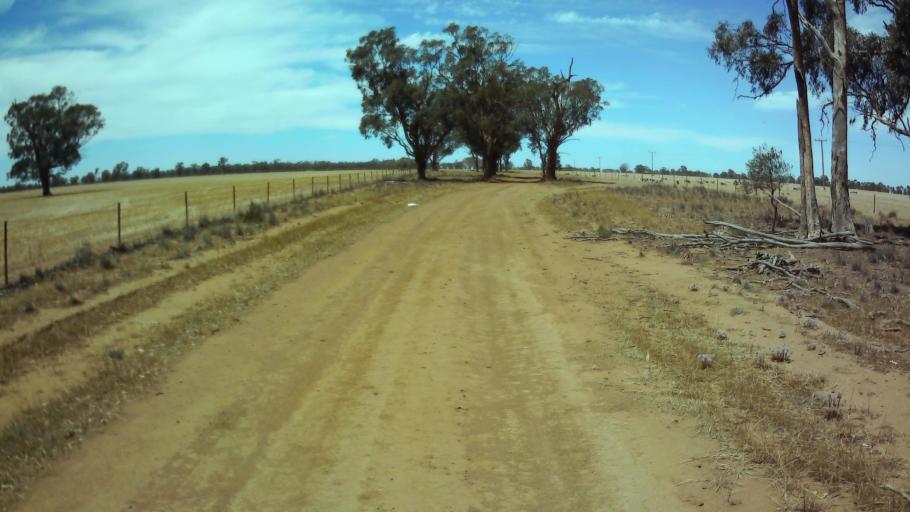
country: AU
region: New South Wales
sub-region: Weddin
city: Grenfell
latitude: -33.8922
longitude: 147.8025
